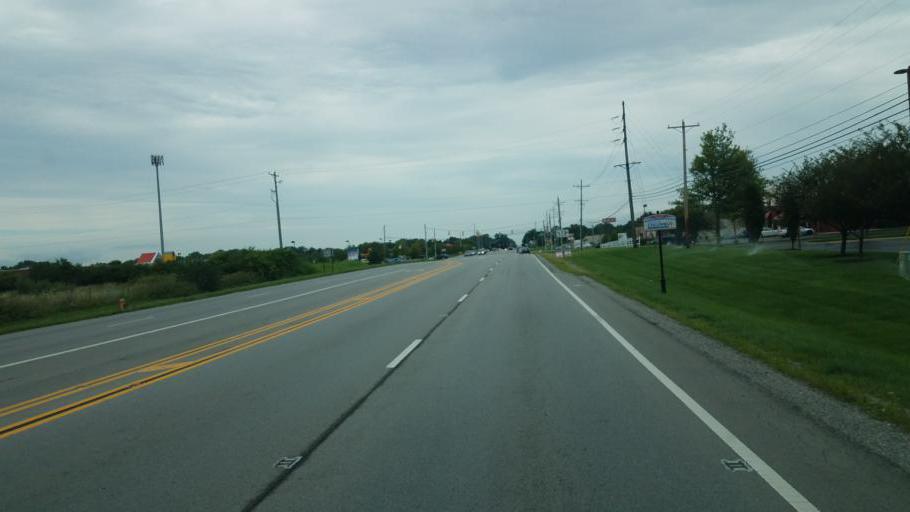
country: US
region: Ohio
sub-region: Franklin County
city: Groveport
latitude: 39.8935
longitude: -82.8826
